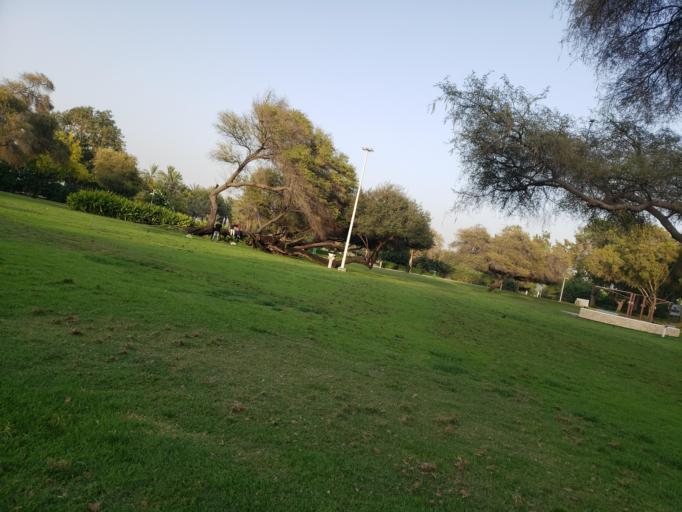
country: AE
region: Ash Shariqah
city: Sharjah
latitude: 25.2348
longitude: 55.3295
